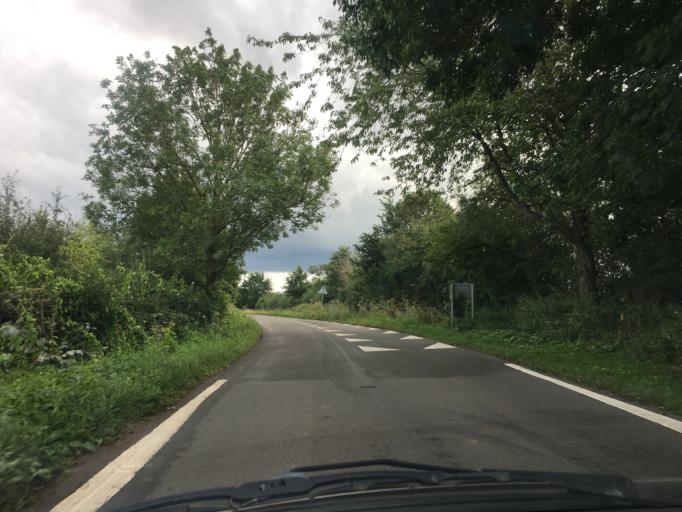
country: GB
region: England
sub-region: Leicestershire
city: Lutterworth
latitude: 52.4885
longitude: -1.2222
